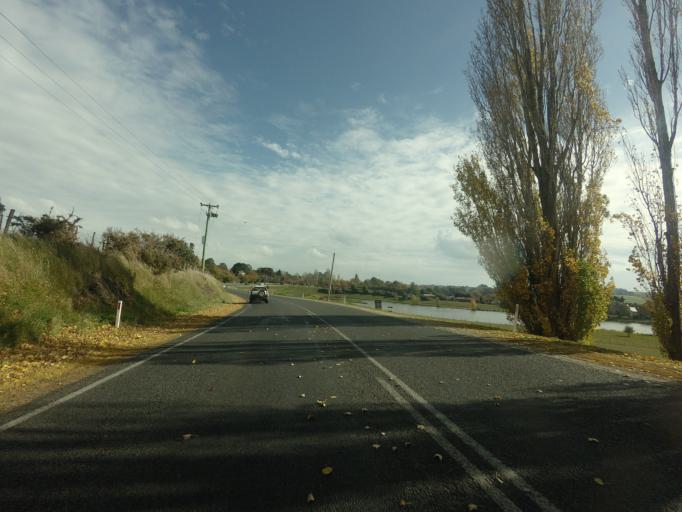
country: AU
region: Tasmania
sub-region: Meander Valley
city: Deloraine
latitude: -41.5246
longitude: 146.6708
